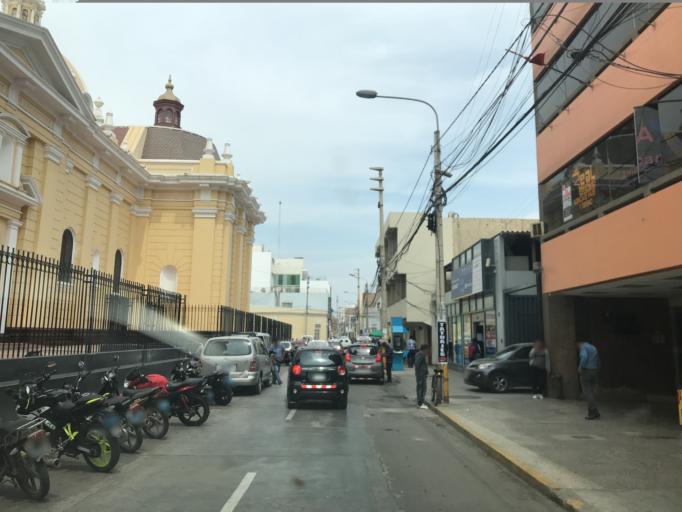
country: PE
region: Lambayeque
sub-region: Provincia de Chiclayo
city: Chiclayo
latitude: -6.7720
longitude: -79.8381
